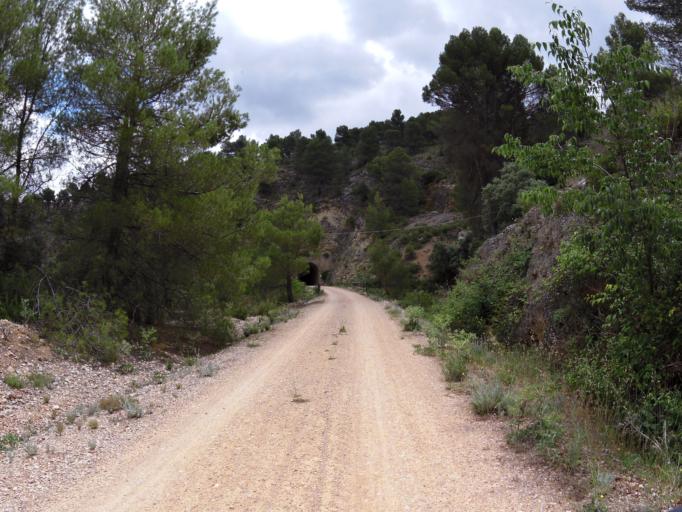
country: ES
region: Castille-La Mancha
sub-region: Provincia de Albacete
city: Casas de Lazaro
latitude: 38.8150
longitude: -2.2798
